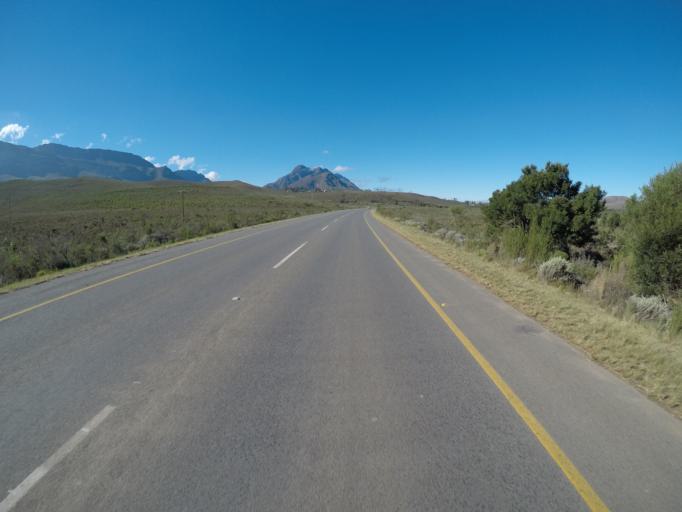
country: ZA
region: Western Cape
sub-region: Overberg District Municipality
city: Caledon
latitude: -34.0491
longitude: 19.5808
